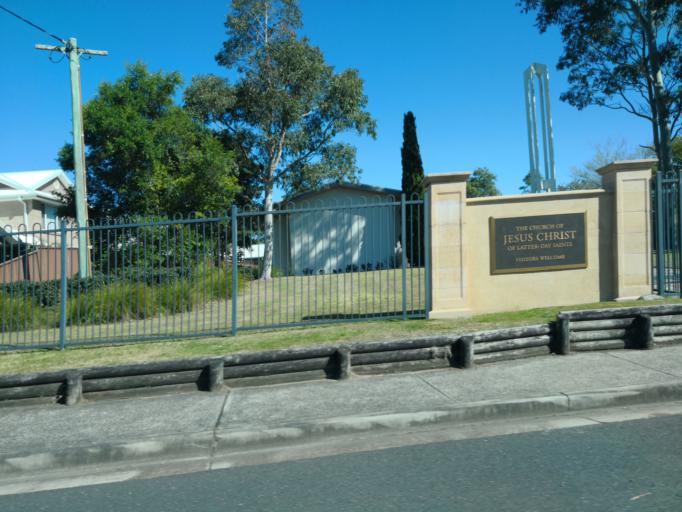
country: AU
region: New South Wales
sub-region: Gosford Shire
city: Narara
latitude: -33.4076
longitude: 151.3507
